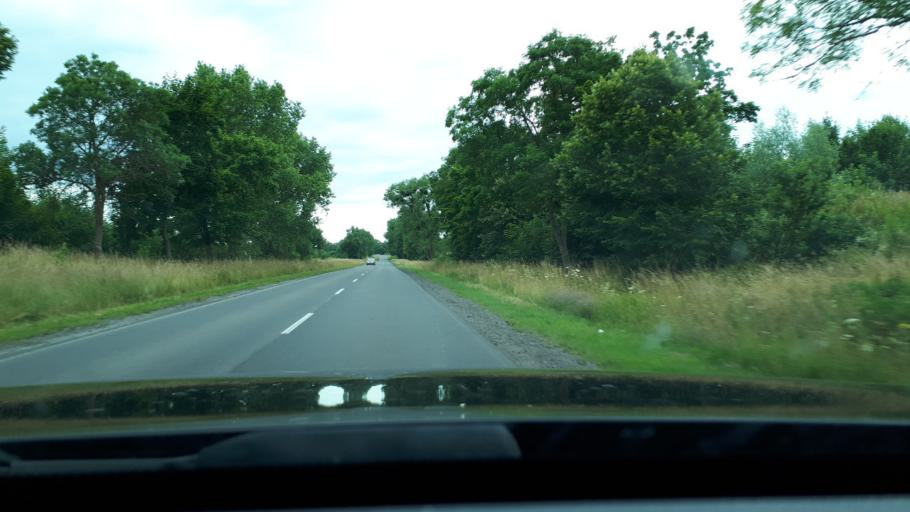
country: PL
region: Warmian-Masurian Voivodeship
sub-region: Powiat olsztynski
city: Olsztynek
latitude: 53.5719
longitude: 20.2721
